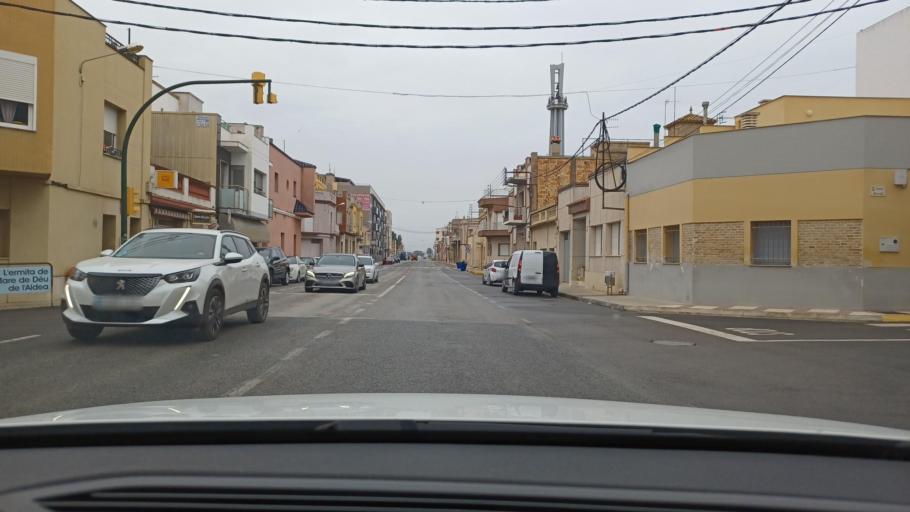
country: ES
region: Catalonia
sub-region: Provincia de Tarragona
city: Amposta
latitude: 40.7412
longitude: 0.6108
